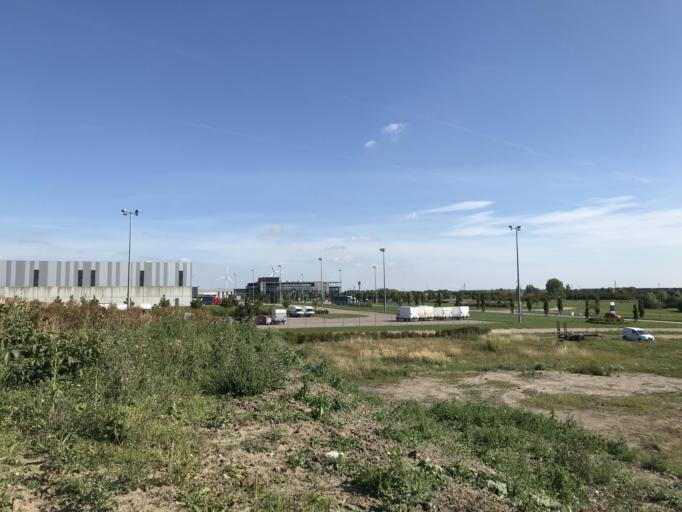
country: SE
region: Skane
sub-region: Landskrona
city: Landskrona
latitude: 55.8779
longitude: 12.8663
